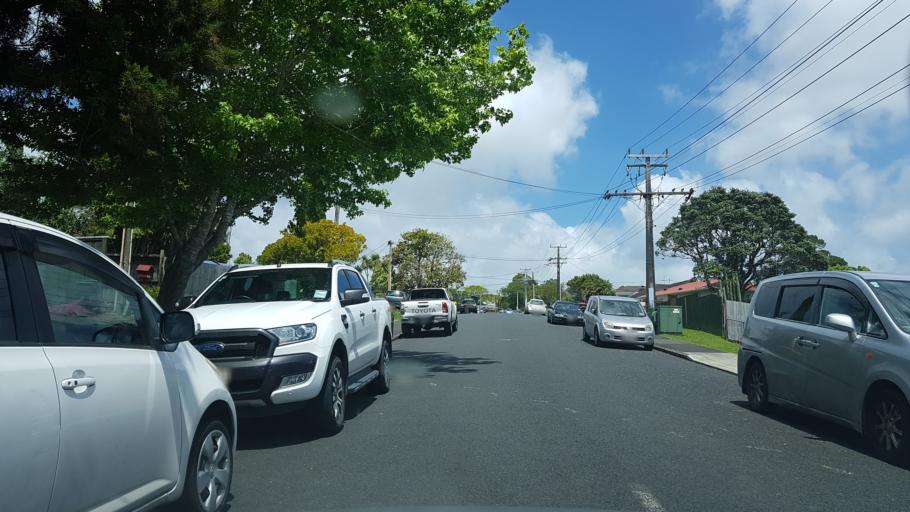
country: NZ
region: Auckland
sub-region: Auckland
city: North Shore
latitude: -36.8056
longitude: 174.7101
